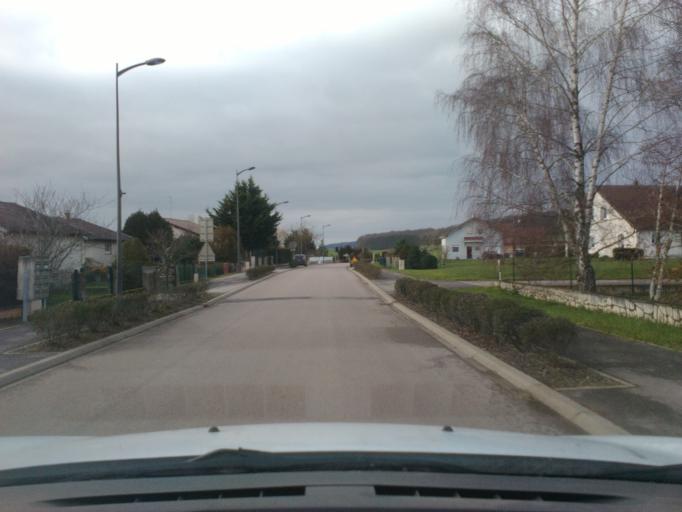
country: FR
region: Lorraine
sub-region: Departement des Vosges
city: Mirecourt
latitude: 48.3352
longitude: 6.0146
